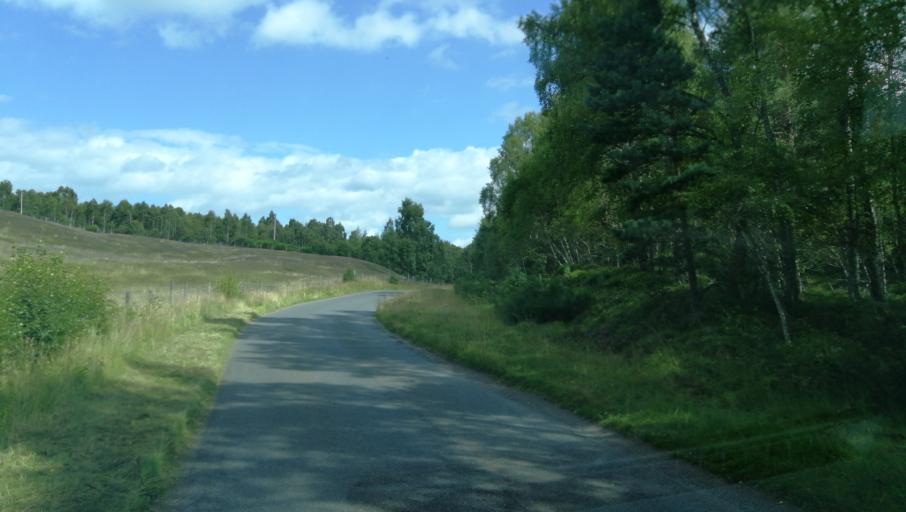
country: GB
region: Scotland
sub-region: Highland
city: Aviemore
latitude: 57.2235
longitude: -3.7571
